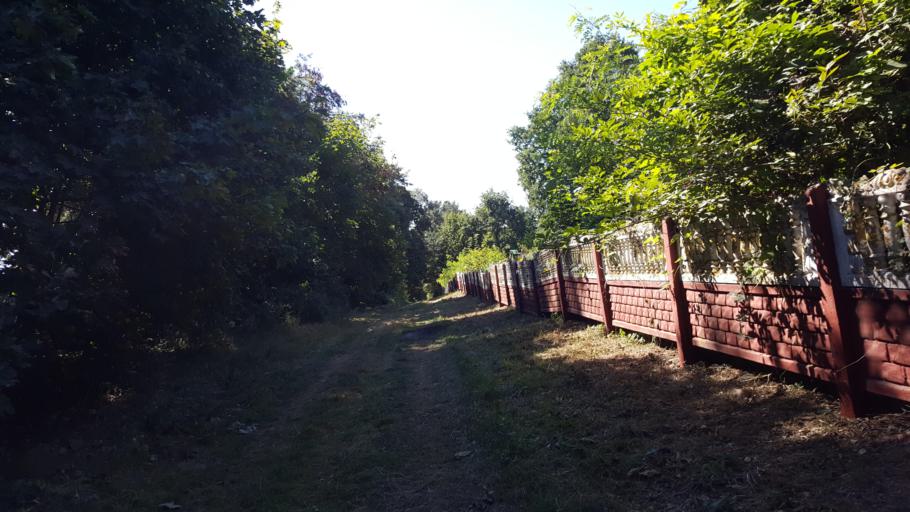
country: PL
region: Lublin Voivodeship
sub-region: Powiat bialski
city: Terespol
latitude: 52.2177
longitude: 23.5108
